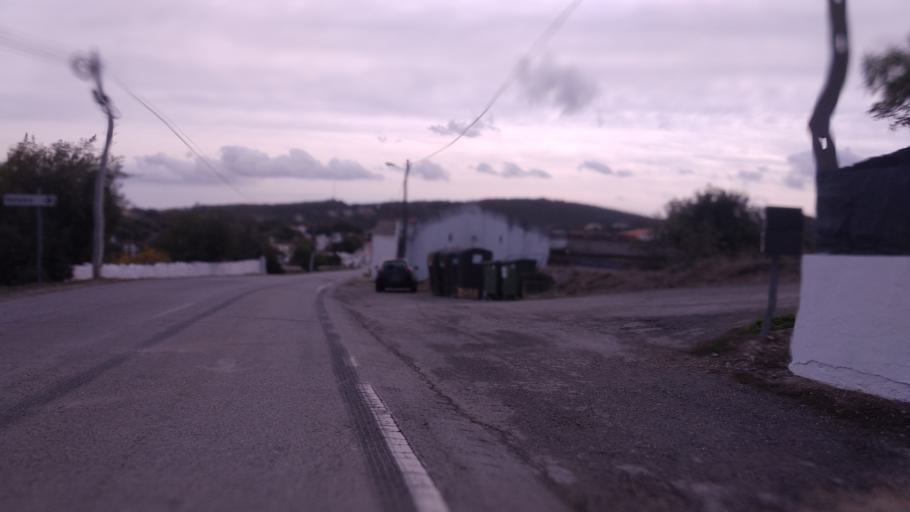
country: PT
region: Faro
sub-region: Sao Bras de Alportel
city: Sao Bras de Alportel
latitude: 37.1776
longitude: -7.9097
